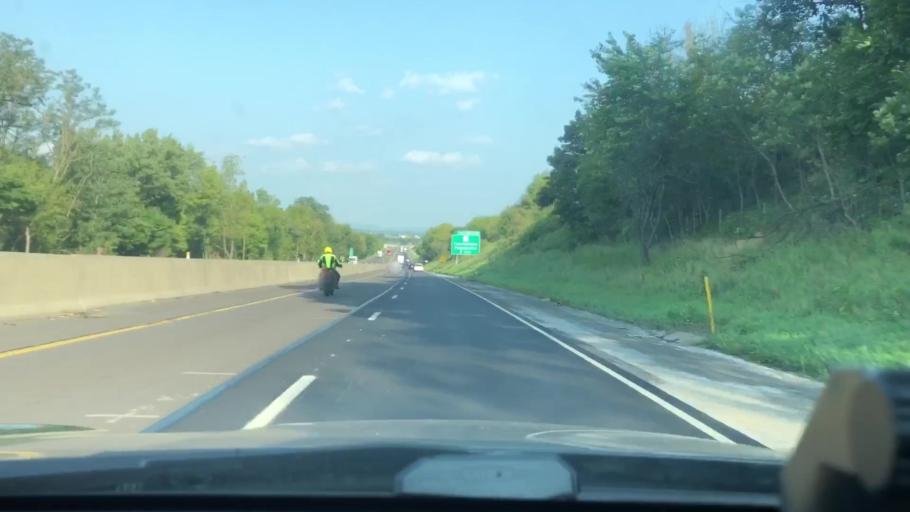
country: US
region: Pennsylvania
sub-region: Lehigh County
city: Breinigsville
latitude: 40.5765
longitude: -75.6705
